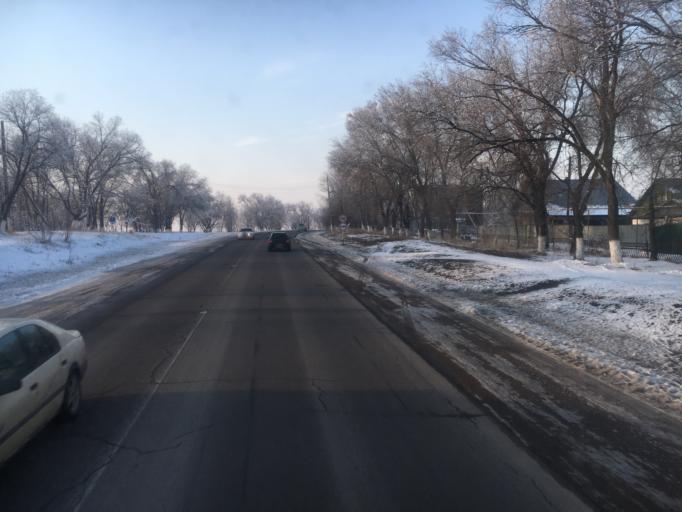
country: KZ
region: Almaty Oblysy
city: Burunday
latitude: 43.3069
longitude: 76.6681
